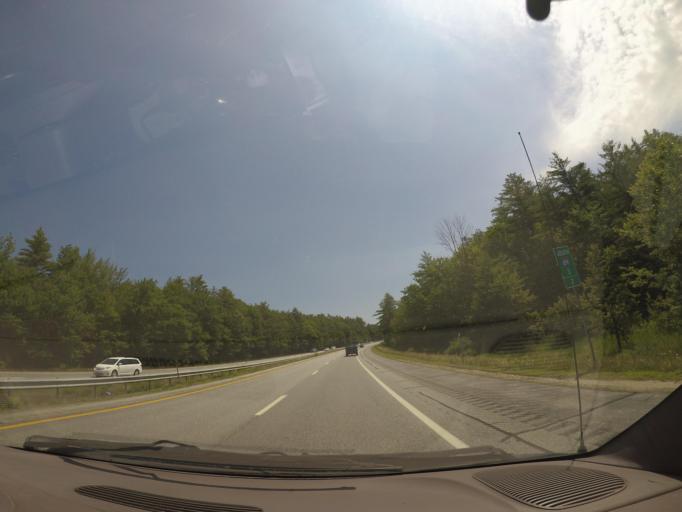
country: US
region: New Hampshire
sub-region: Merrimack County
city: Concord
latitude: 43.1848
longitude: -71.5873
